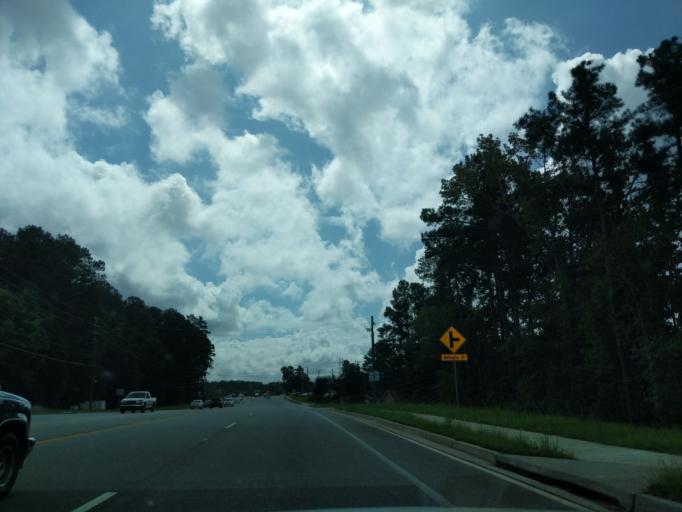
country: US
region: Georgia
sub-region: Columbia County
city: Evans
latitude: 33.5518
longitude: -82.1545
